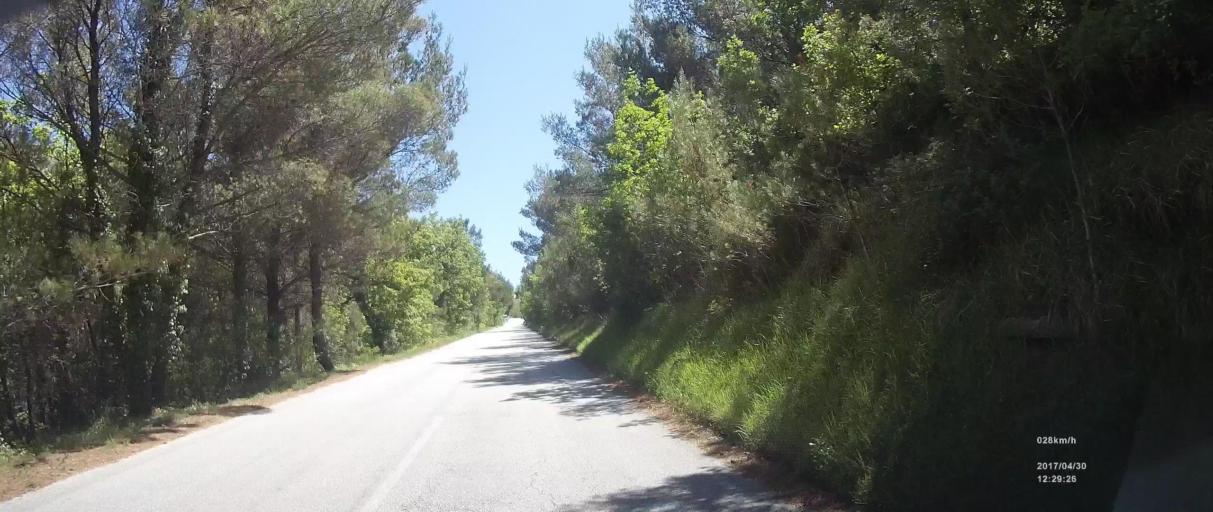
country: HR
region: Splitsko-Dalmatinska
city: Srinjine
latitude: 43.5029
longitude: 16.5989
